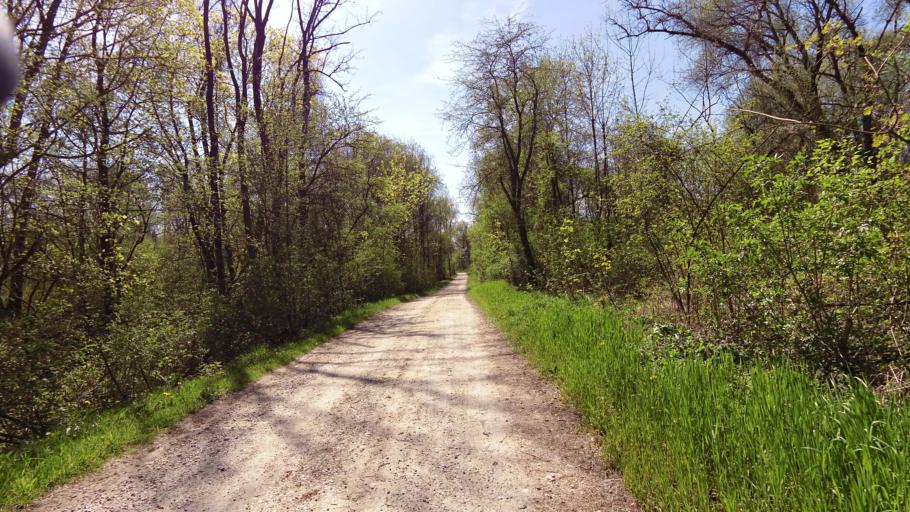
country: DE
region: Bavaria
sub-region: Lower Bavaria
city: Ergolding
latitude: 48.5616
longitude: 12.1863
